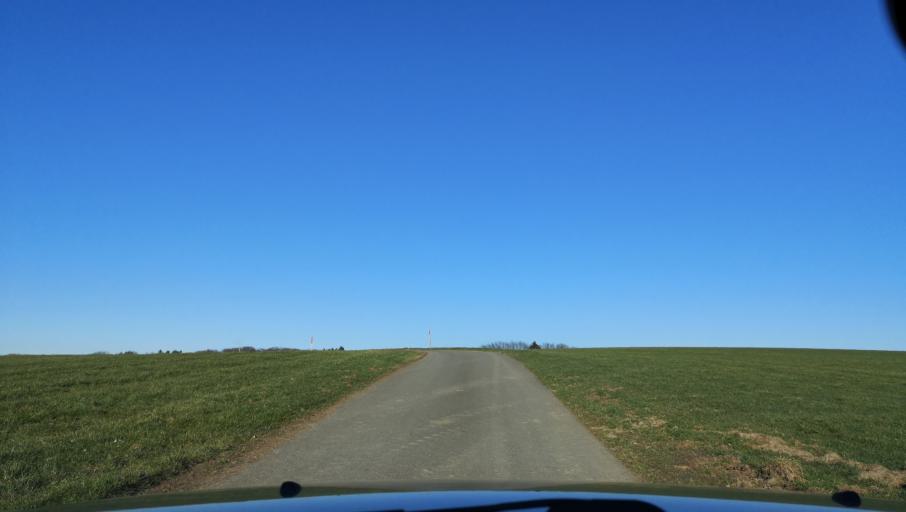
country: DE
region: North Rhine-Westphalia
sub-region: Regierungsbezirk Arnsberg
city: Breckerfeld
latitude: 51.2233
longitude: 7.4192
